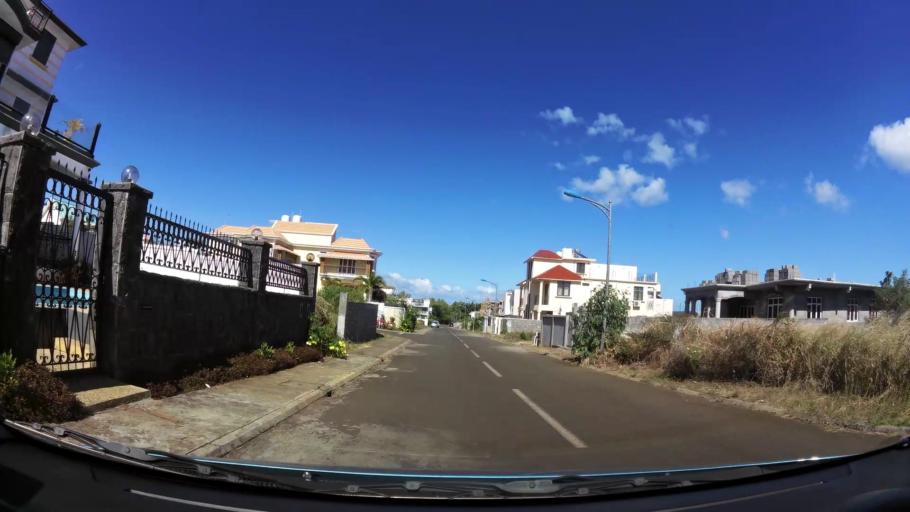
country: MU
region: Black River
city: Flic en Flac
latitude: -20.2837
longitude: 57.3747
